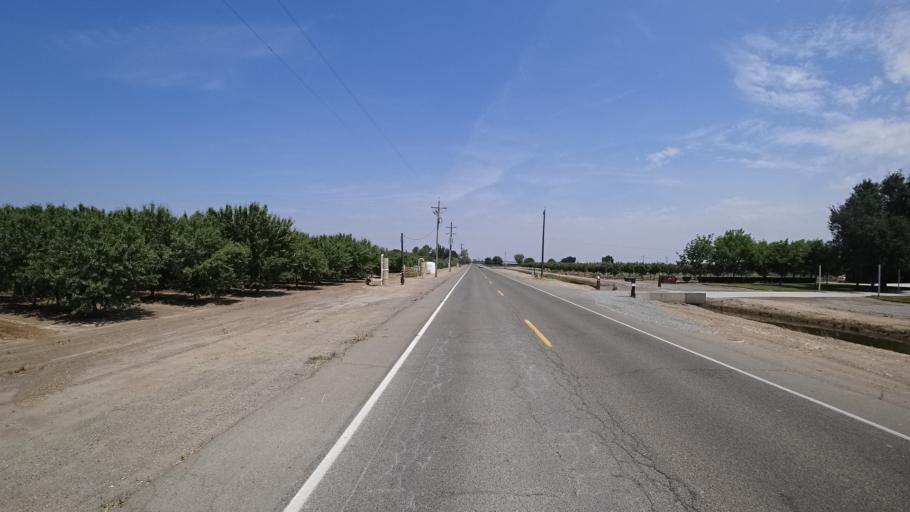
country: US
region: California
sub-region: Kings County
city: Lemoore
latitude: 36.3358
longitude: -119.7808
